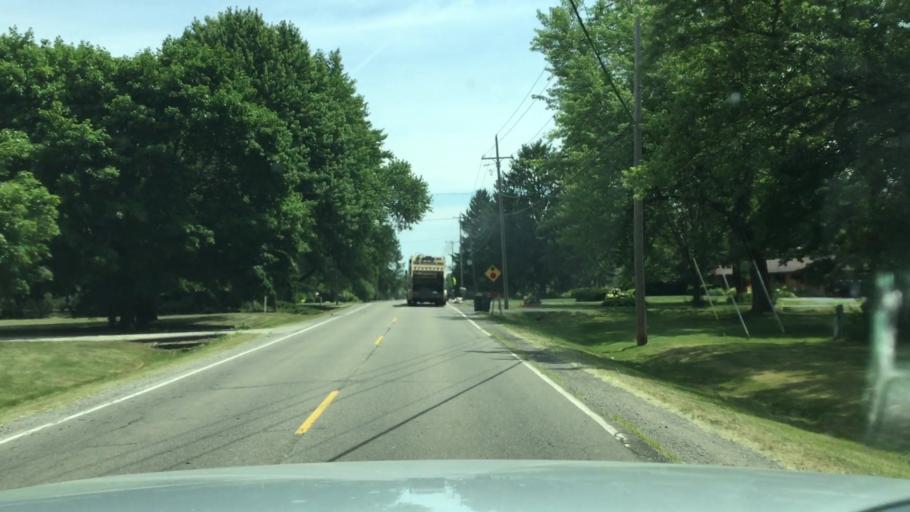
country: US
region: Michigan
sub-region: Genesee County
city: Swartz Creek
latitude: 43.0165
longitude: -83.7864
